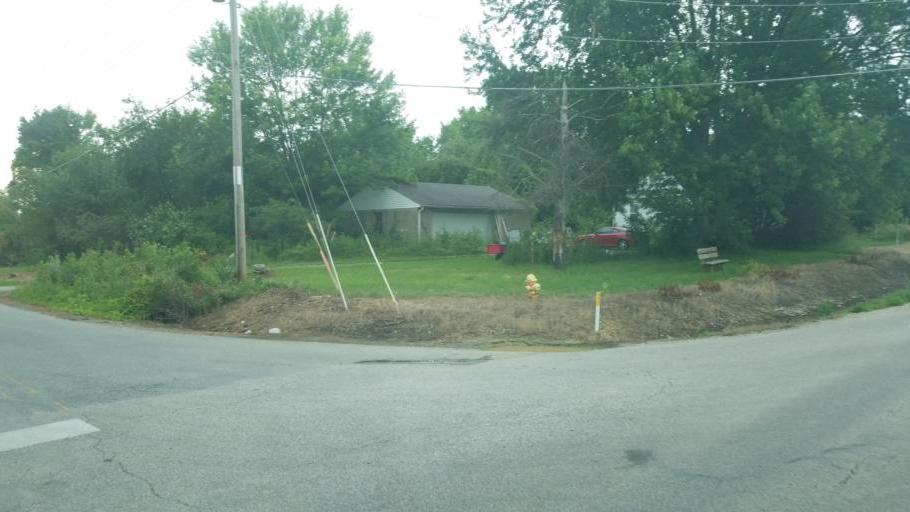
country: US
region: Ohio
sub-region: Delaware County
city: Sunbury
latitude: 40.2877
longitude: -82.8497
